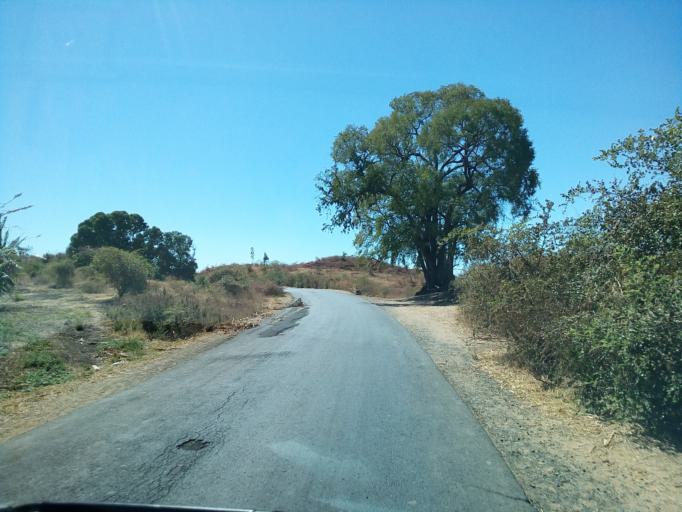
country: MG
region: Boeny
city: Ambato Boeny
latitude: -16.3827
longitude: 46.9345
